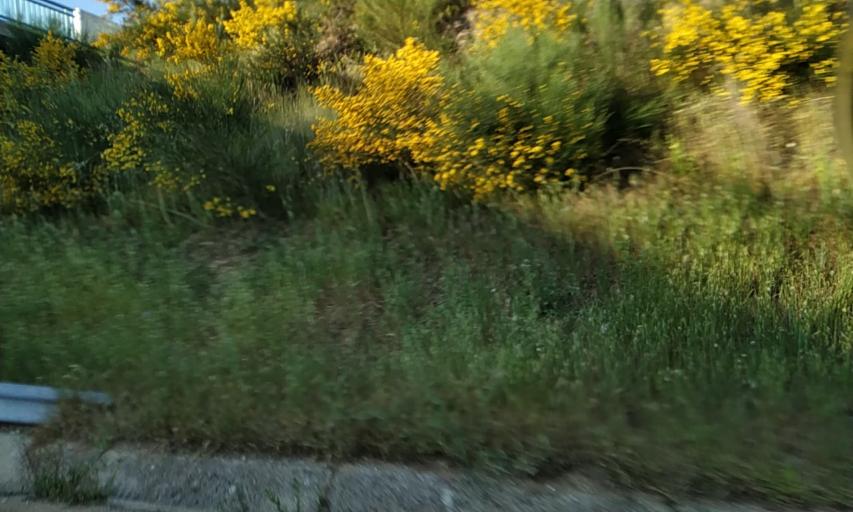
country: PT
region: Portalegre
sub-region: Portalegre
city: Portalegre
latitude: 39.3055
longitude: -7.4413
